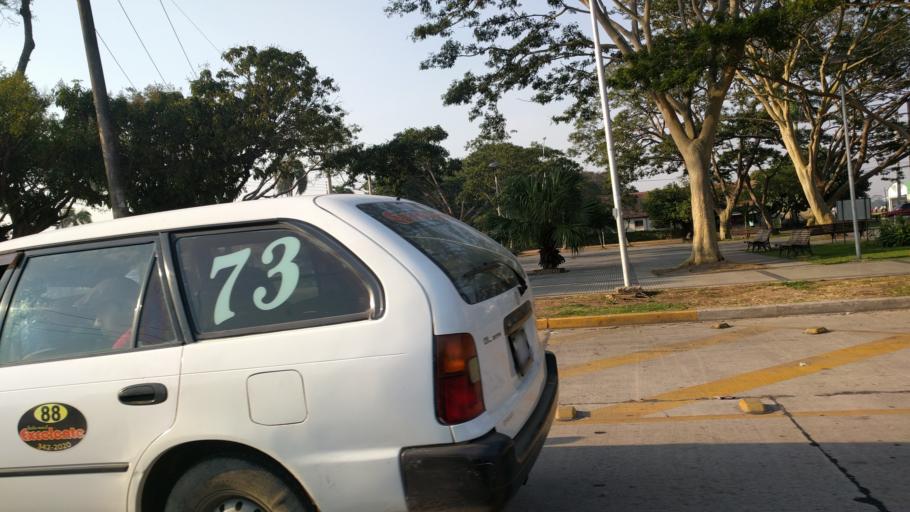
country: BO
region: Santa Cruz
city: Santa Cruz de la Sierra
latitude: -17.7986
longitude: -63.1768
